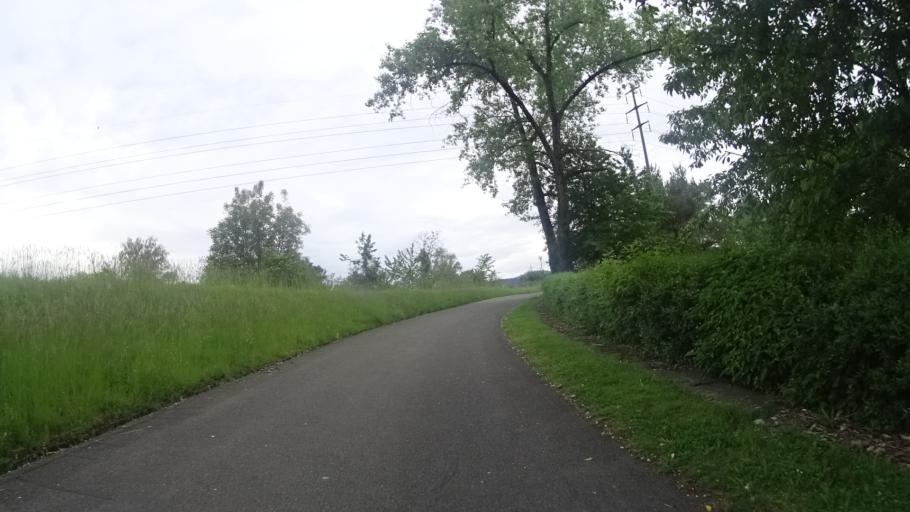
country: CH
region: Aargau
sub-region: Bezirk Zurzach
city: Koblenz
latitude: 47.5963
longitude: 8.2275
